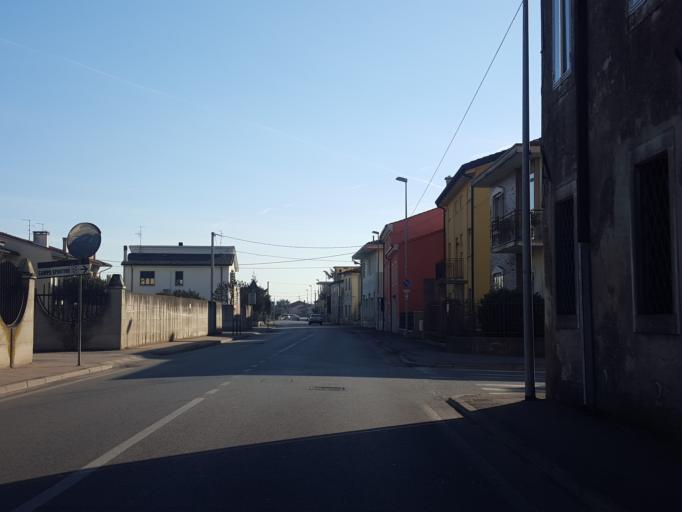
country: IT
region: Veneto
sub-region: Provincia di Verona
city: Locara
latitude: 45.3987
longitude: 11.3316
